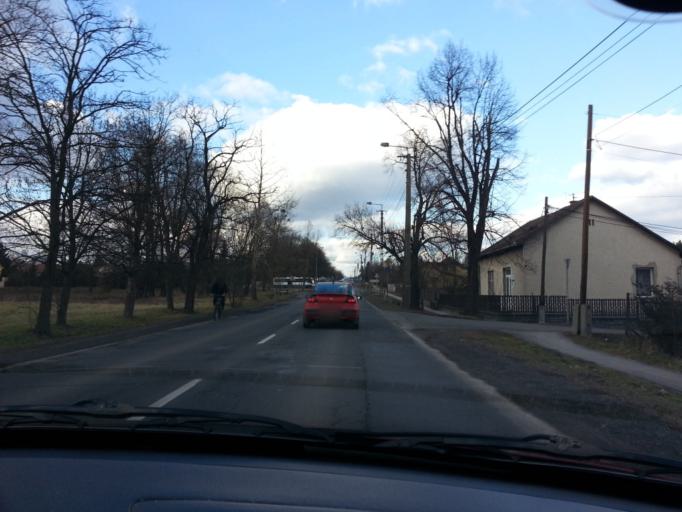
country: HU
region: Nograd
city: Batonyterenye
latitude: 48.0132
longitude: 19.8228
